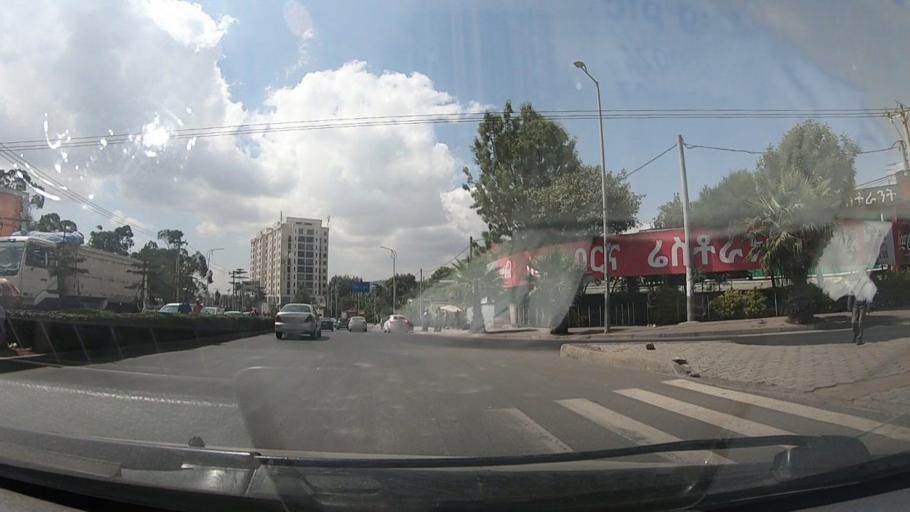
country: ET
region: Adis Abeba
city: Addis Ababa
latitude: 8.9886
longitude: 38.7230
